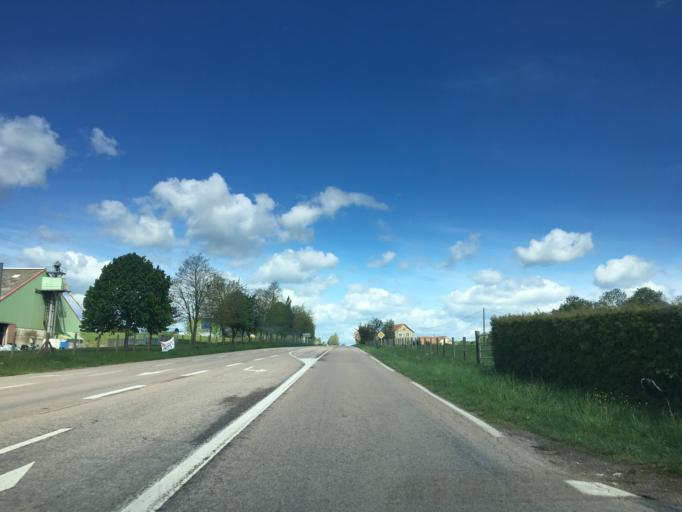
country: FR
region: Lower Normandy
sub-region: Departement de l'Orne
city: Rai
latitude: 48.7906
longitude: 0.5970
